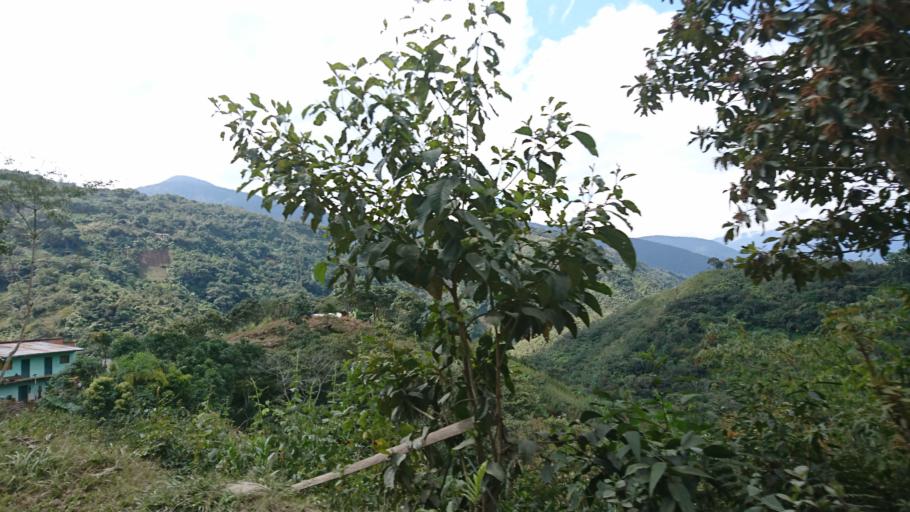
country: BO
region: La Paz
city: Coroico
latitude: -16.0823
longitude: -67.7888
